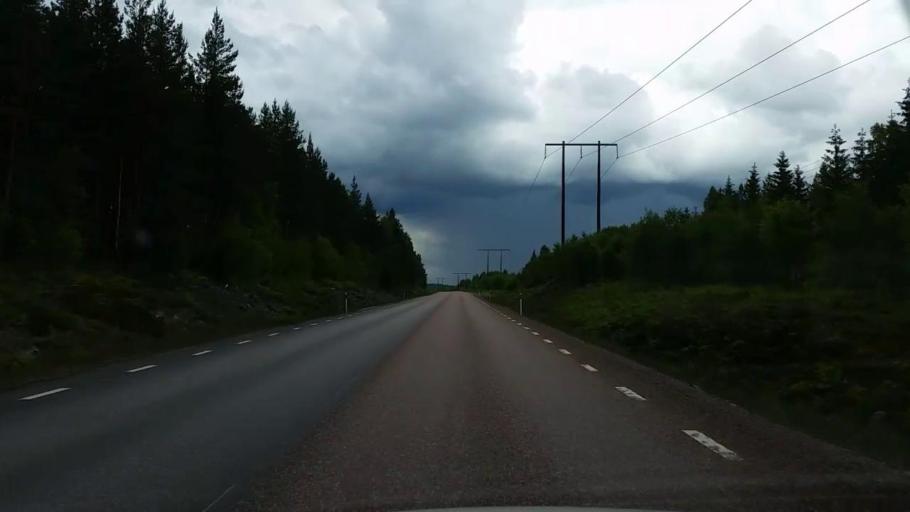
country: SE
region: Gaevleborg
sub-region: Hofors Kommun
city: Hofors
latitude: 60.5275
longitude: 16.4537
